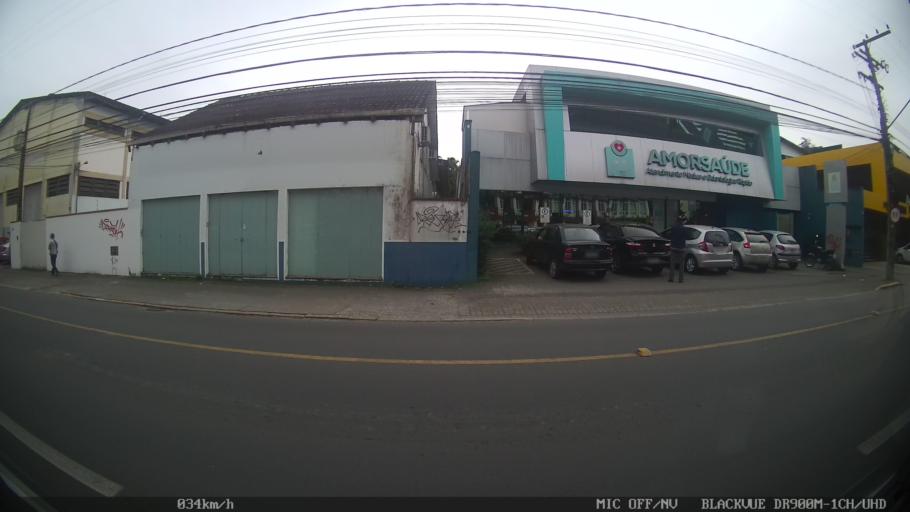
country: BR
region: Santa Catarina
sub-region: Joinville
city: Joinville
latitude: -26.2940
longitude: -48.8410
